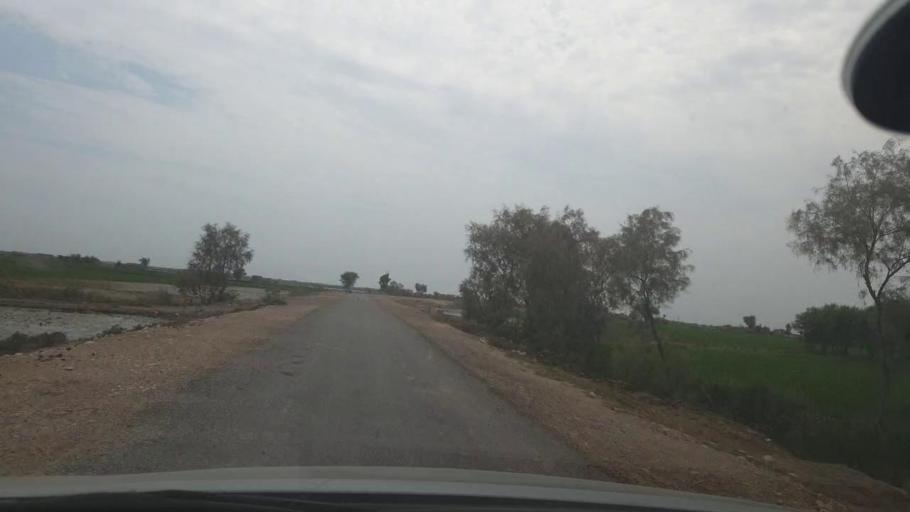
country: PK
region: Balochistan
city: Garhi Khairo
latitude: 28.0201
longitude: 68.0445
